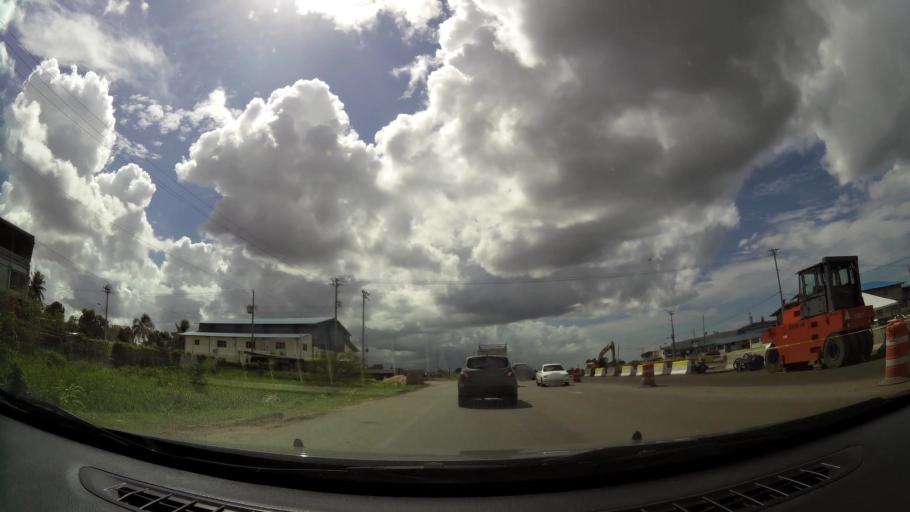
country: TT
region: City of San Fernando
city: San Fernando
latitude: 10.2480
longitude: -61.4895
